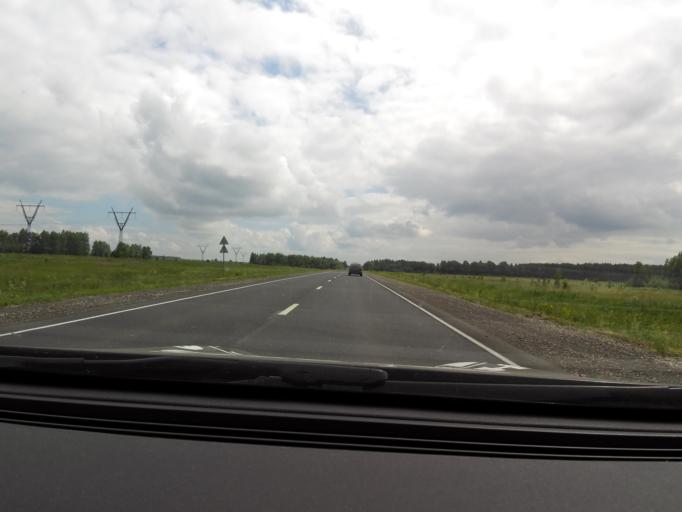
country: RU
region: Perm
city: Orda
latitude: 57.2552
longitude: 57.0336
